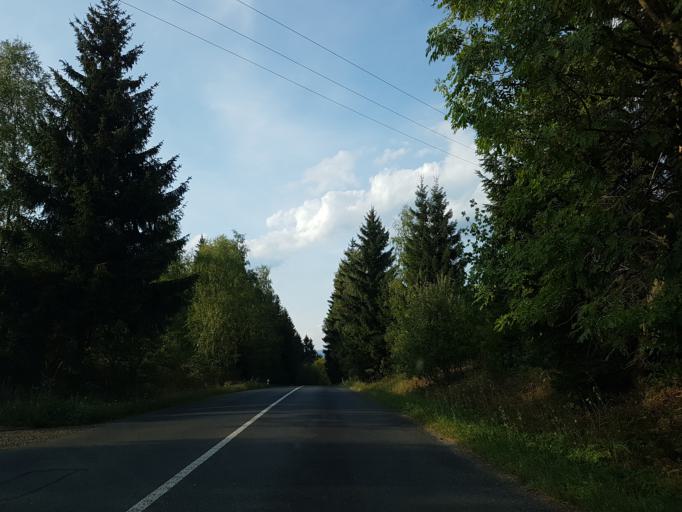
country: CZ
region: Liberecky
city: Mala Skala
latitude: 50.6625
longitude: 15.1682
